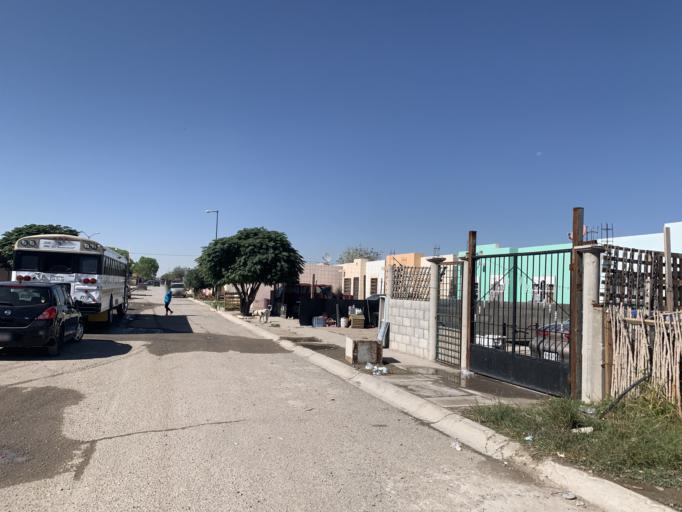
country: US
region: Texas
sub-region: El Paso County
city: San Elizario
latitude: 31.5877
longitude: -106.3370
